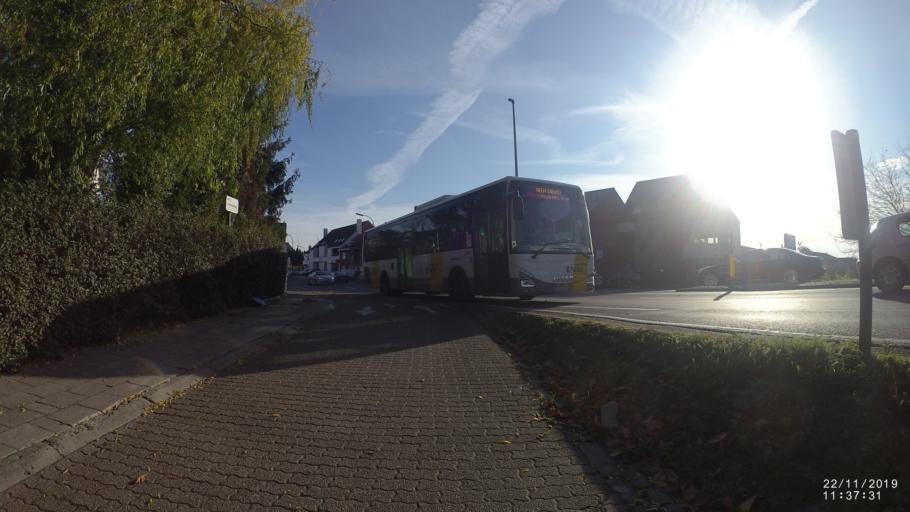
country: BE
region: Flanders
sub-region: Provincie Limburg
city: Hasselt
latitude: 50.9438
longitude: 5.3440
